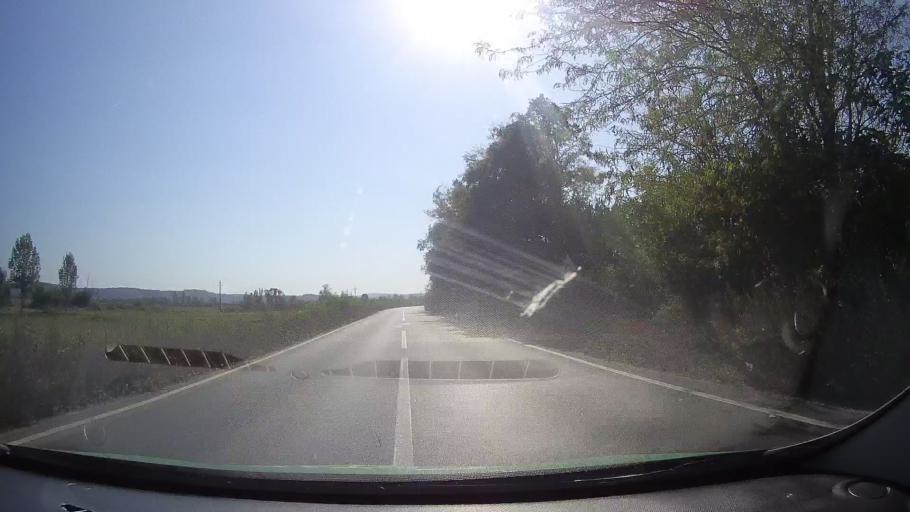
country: RO
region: Arad
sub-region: Comuna Ususau
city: Ususau
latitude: 46.1023
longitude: 21.8149
